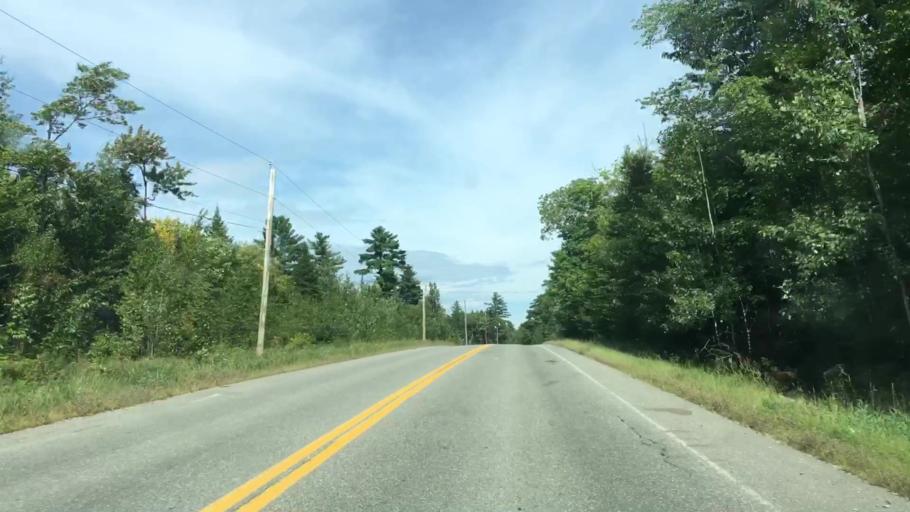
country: US
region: Maine
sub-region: Penobscot County
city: Lincoln
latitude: 45.3725
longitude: -68.5555
